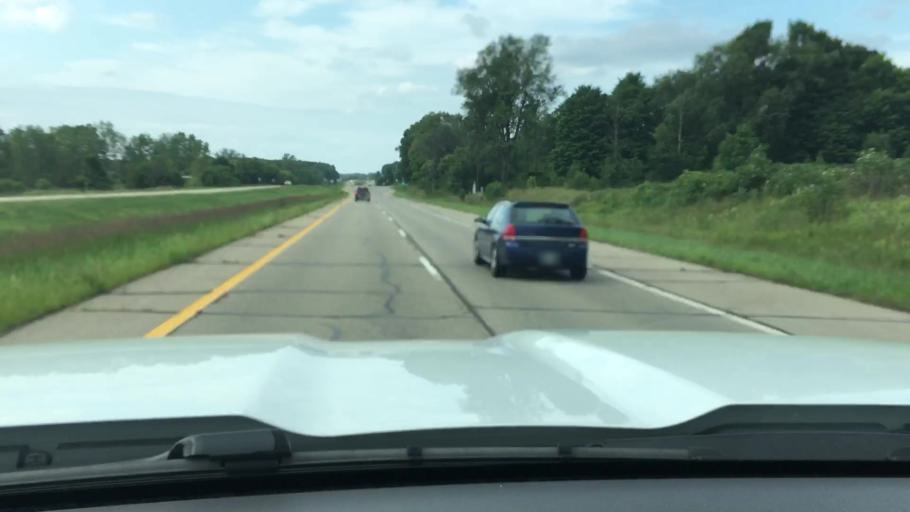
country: US
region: Michigan
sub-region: Eaton County
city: Dimondale
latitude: 42.6223
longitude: -84.6225
